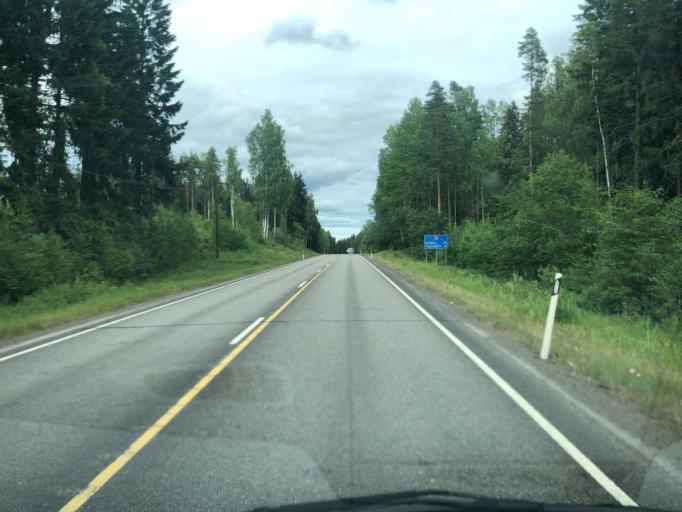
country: FI
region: Kymenlaakso
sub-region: Kouvola
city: Kouvola
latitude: 60.9530
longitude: 26.8539
